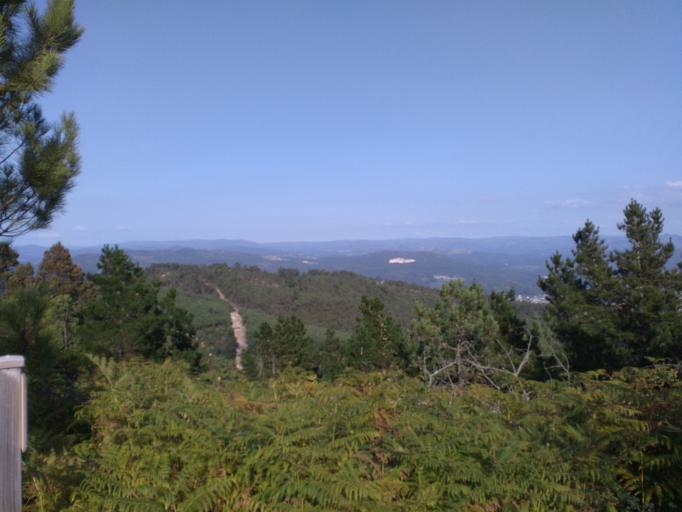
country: ES
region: Galicia
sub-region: Provincia de Pontevedra
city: Marin
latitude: 42.3536
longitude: -8.6746
